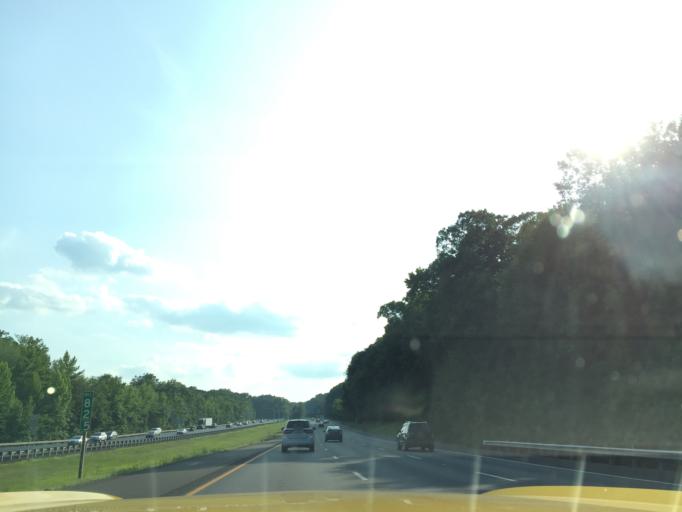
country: US
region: Maryland
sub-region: Harford County
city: Perryman
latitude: 39.5046
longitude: -76.2181
